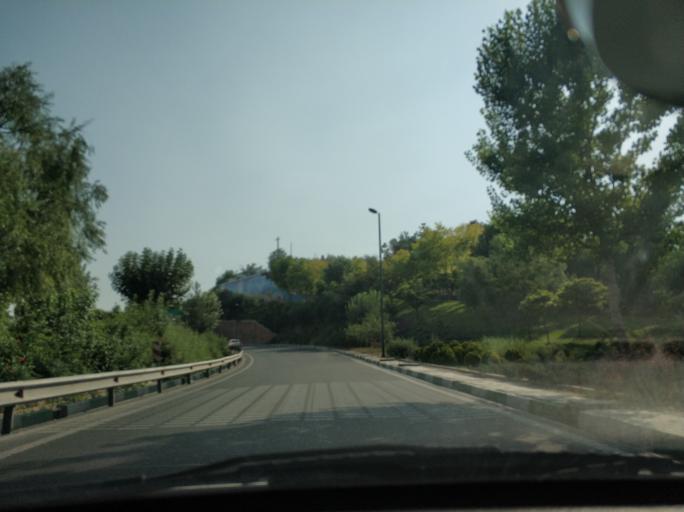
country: IR
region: Tehran
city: Tehran
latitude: 35.7414
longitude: 51.3687
